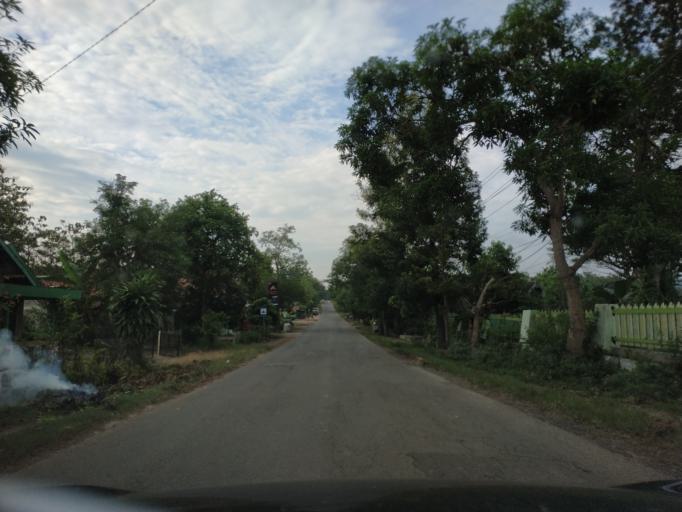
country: ID
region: Central Java
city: Medang
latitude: -6.9115
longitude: 111.4396
